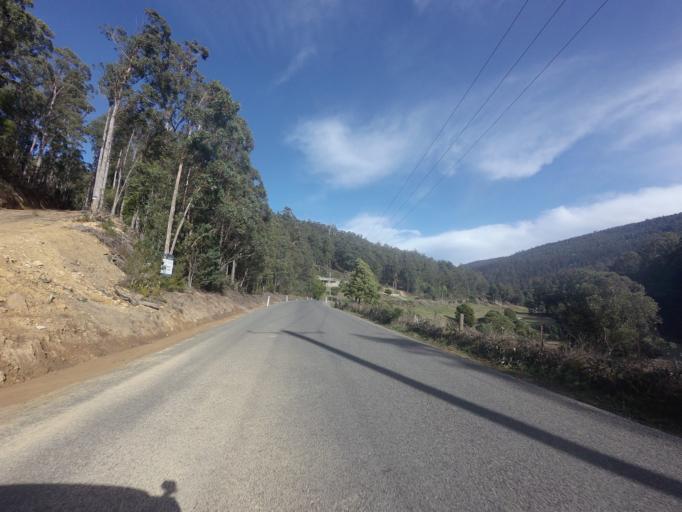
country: AU
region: Tasmania
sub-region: Huon Valley
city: Huonville
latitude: -43.0430
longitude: 147.1249
